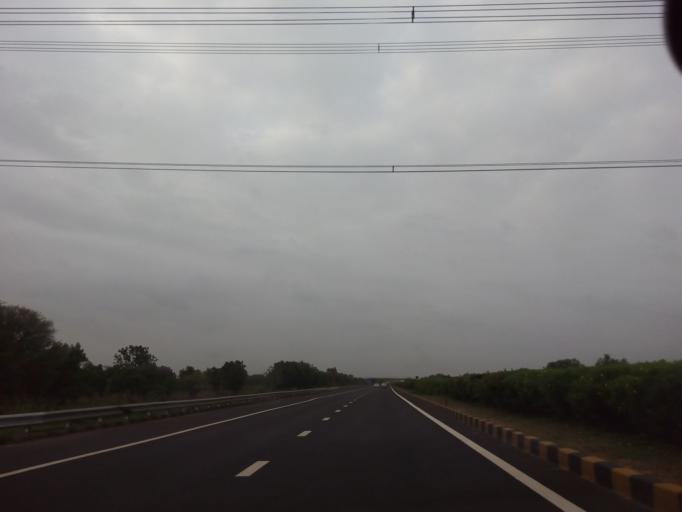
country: IN
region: Gujarat
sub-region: Kheda
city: Nadiad
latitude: 22.7581
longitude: 72.8566
